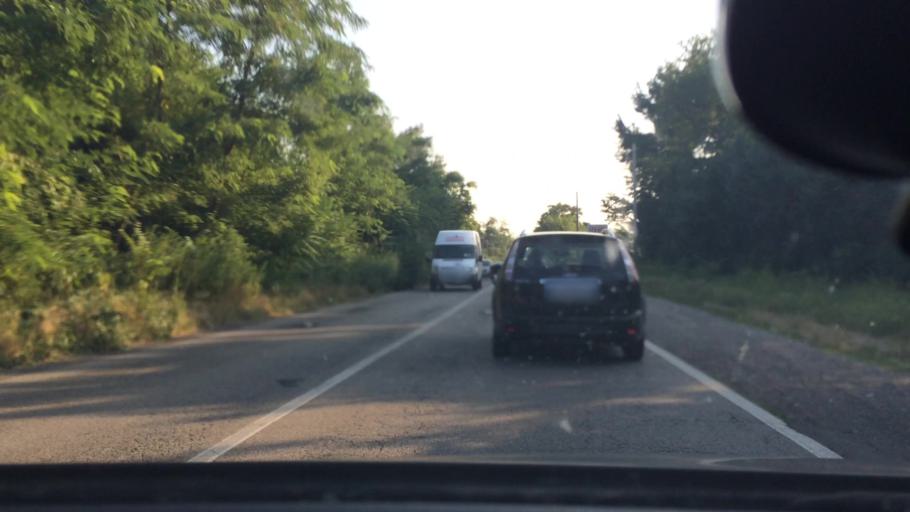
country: IT
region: Lombardy
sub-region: Citta metropolitana di Milano
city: Mantegazza
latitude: 45.5264
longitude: 8.9718
